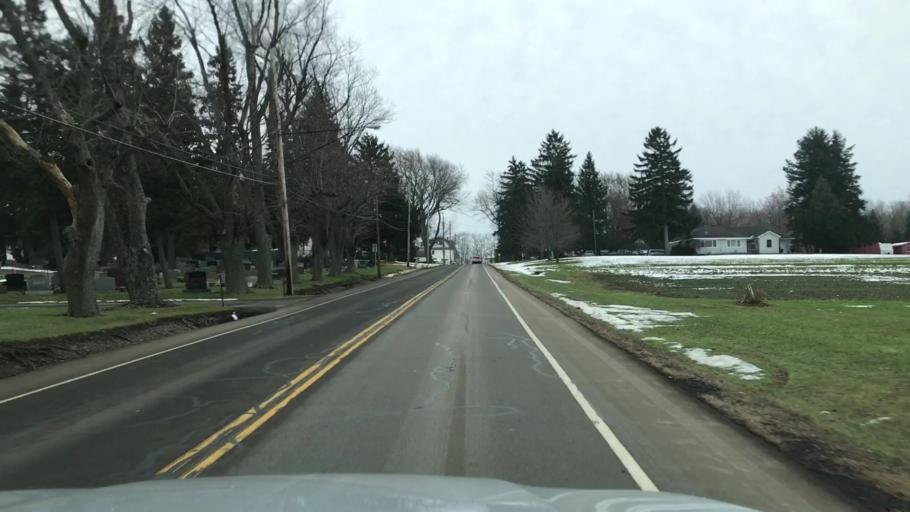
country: US
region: New York
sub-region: Erie County
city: Hamburg
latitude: 42.7430
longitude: -78.8016
